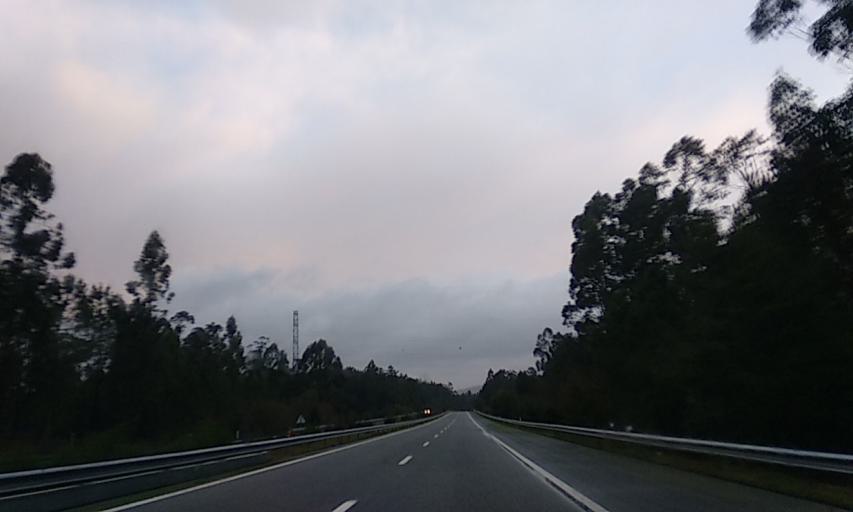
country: PT
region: Braga
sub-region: Barcelos
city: Galegos
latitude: 41.6349
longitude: -8.5611
